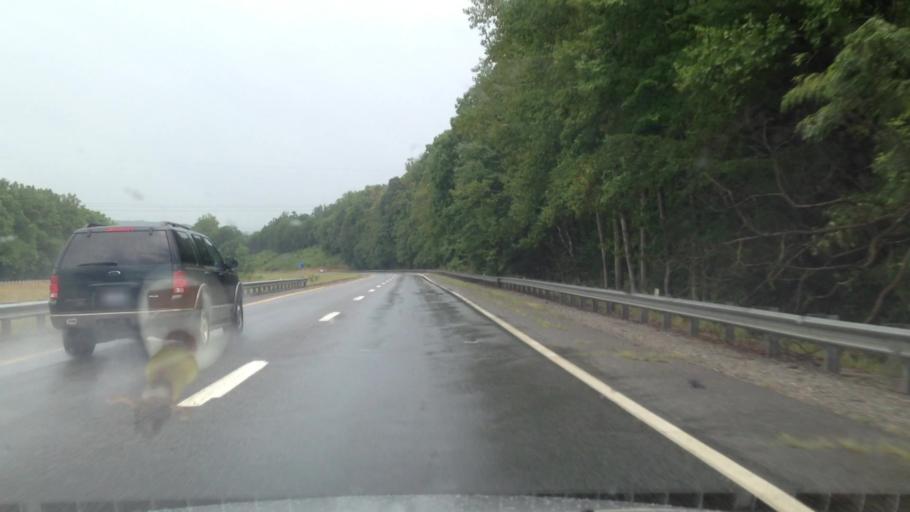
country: US
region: Virginia
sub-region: Henry County
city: Stanleytown
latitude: 36.7080
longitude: -79.9574
